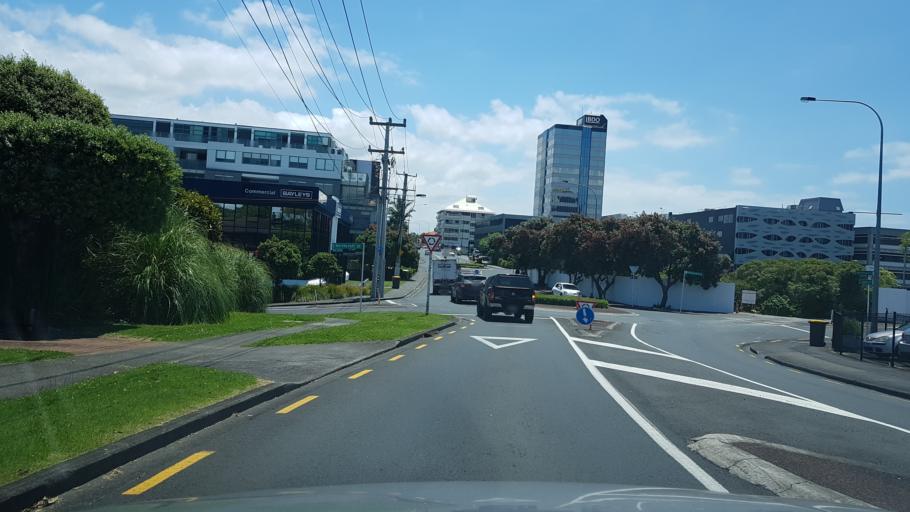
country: NZ
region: Auckland
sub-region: Auckland
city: North Shore
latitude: -36.7908
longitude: 174.7700
